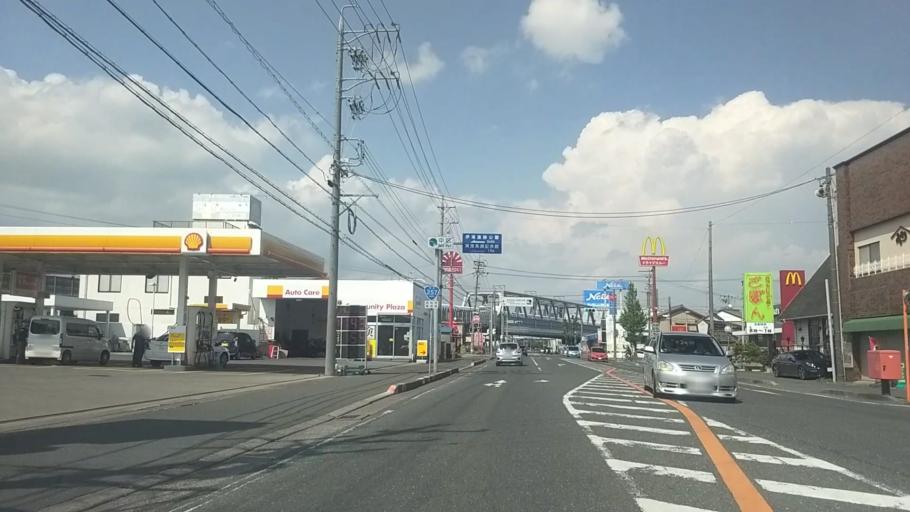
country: JP
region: Shizuoka
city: Hamamatsu
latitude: 34.6928
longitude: 137.7175
